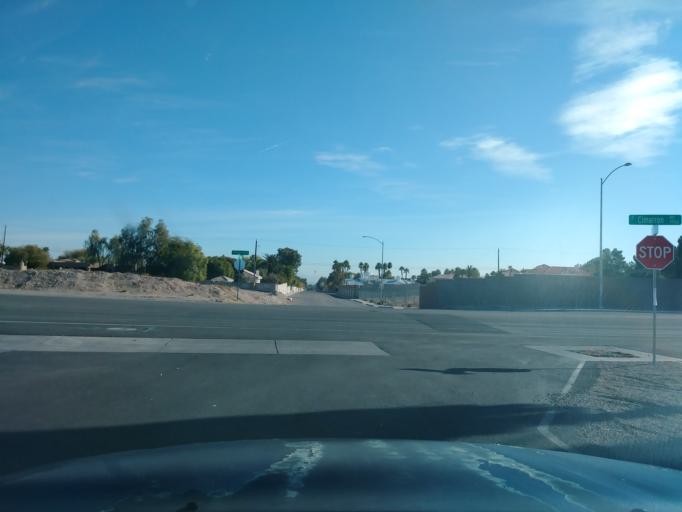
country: US
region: Nevada
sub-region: Clark County
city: Spring Valley
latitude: 36.1496
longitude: -115.2707
